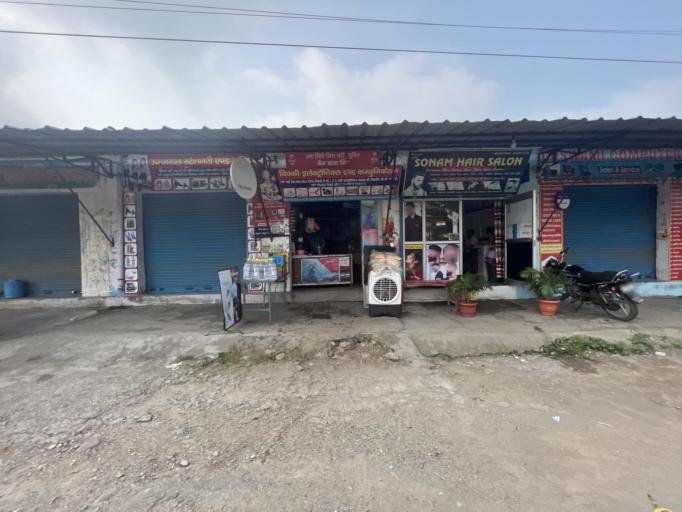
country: IN
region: Uttarakhand
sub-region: Naini Tal
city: Haldwani
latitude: 29.1944
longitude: 79.4998
